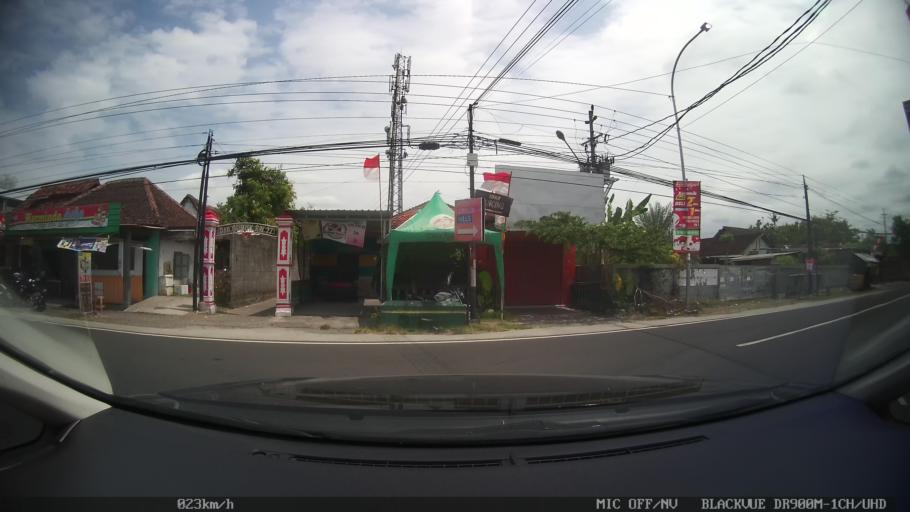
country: ID
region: Central Java
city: Candi Prambanan
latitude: -7.7817
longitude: 110.4827
